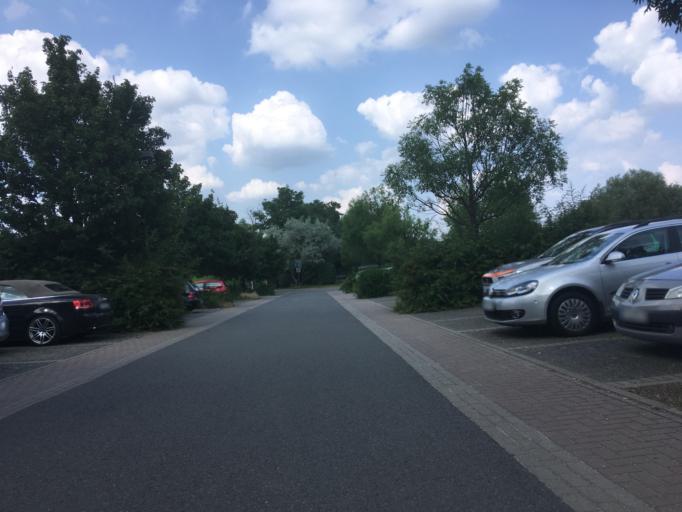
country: DE
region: Brandenburg
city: Wildau
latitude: 52.3259
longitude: 13.6228
